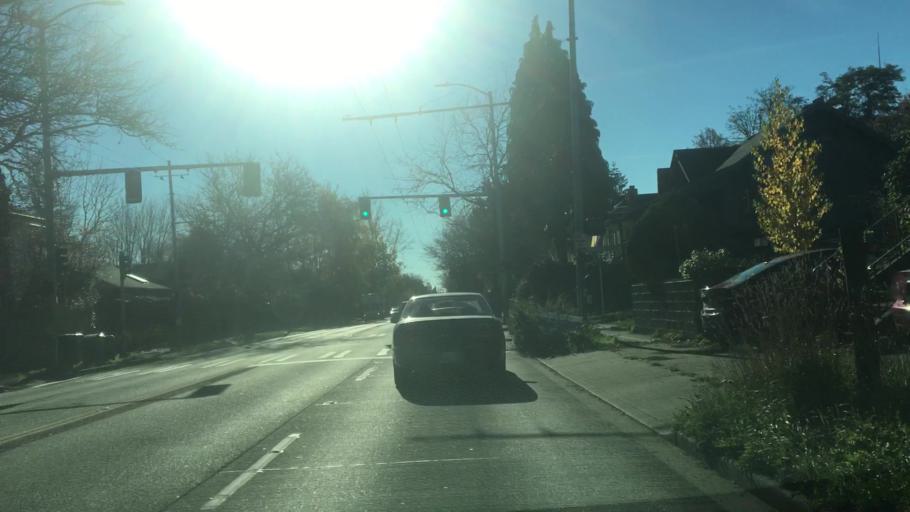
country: US
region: Washington
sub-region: King County
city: Seattle
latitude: 47.6235
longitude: -122.3025
